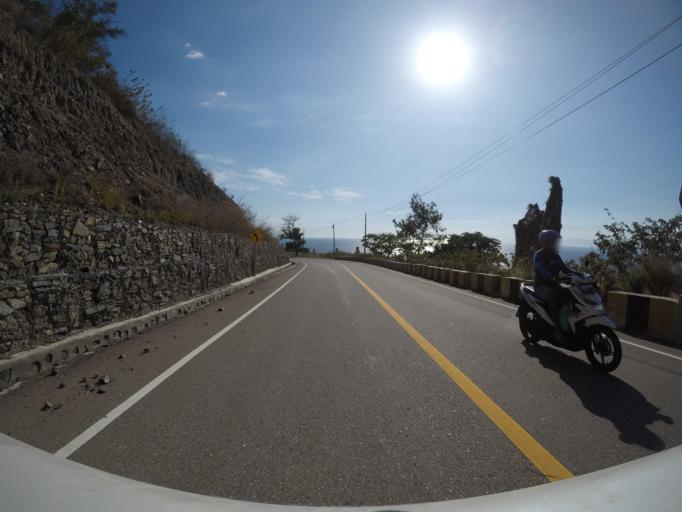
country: TL
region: Liquica
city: Maubara
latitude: -8.6518
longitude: 125.1209
